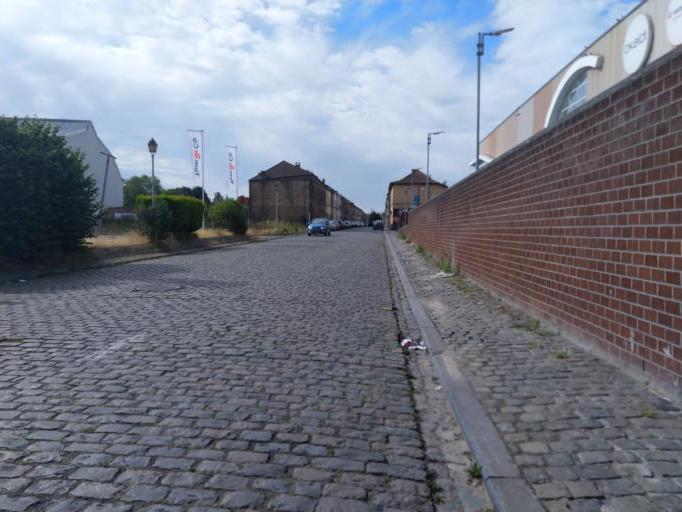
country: BE
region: Wallonia
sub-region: Province du Hainaut
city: Saint-Ghislain
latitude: 50.4389
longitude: 3.8401
